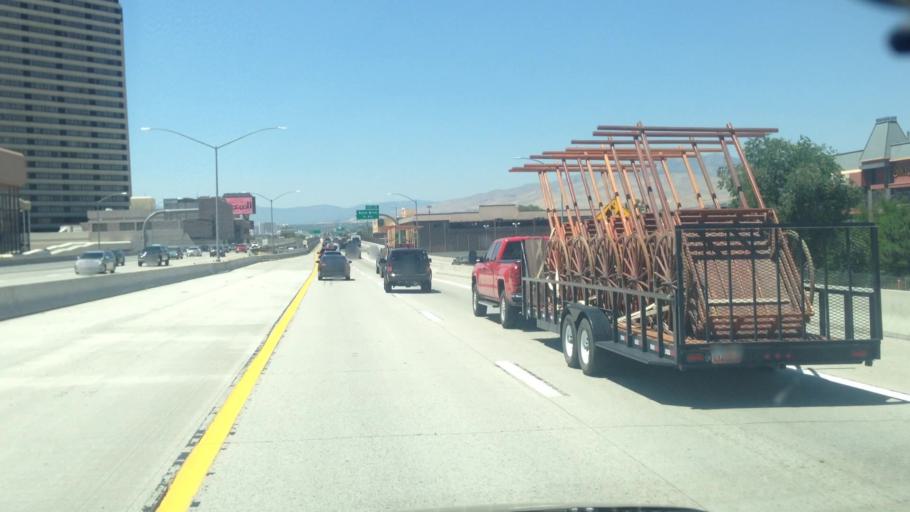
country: US
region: Nevada
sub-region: Washoe County
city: Sparks
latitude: 39.5344
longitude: -119.7549
